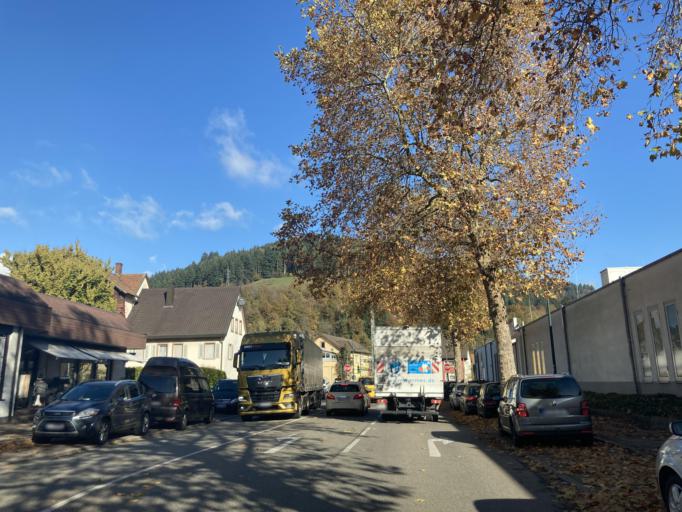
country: DE
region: Baden-Wuerttemberg
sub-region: Freiburg Region
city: Hofstetten
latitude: 48.2787
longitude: 8.0903
